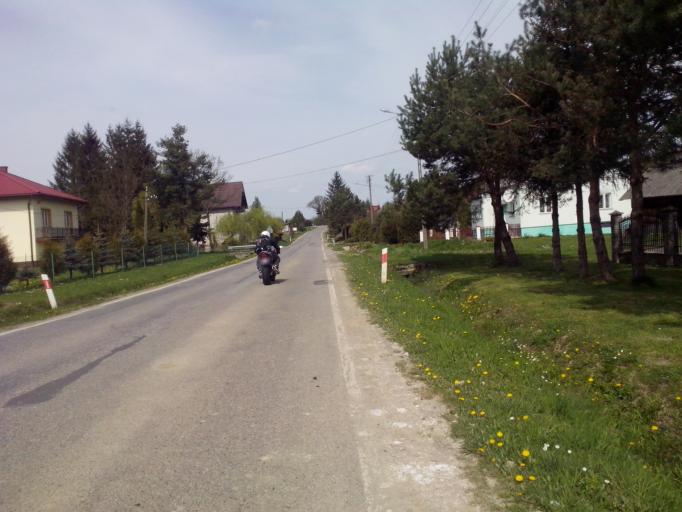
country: PL
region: Subcarpathian Voivodeship
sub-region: Powiat strzyzowski
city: Jawornik
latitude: 49.8053
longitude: 21.8577
